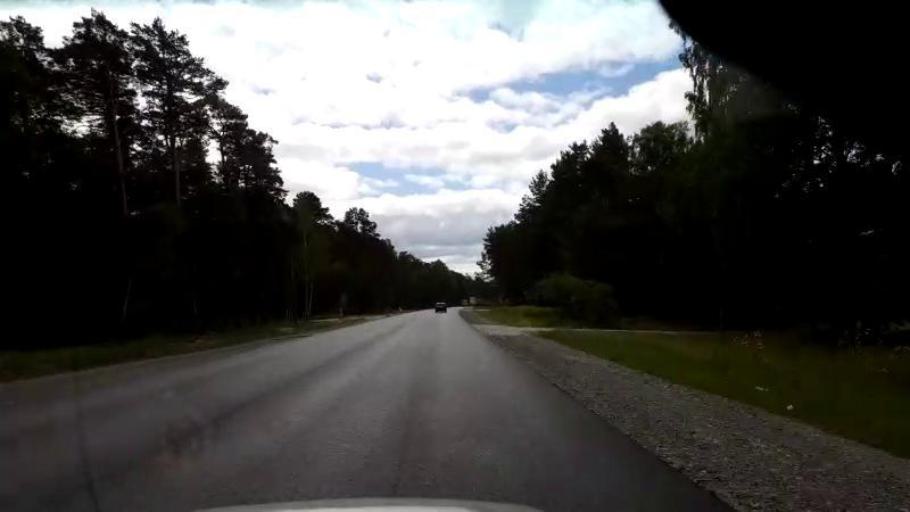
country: LV
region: Salacgrivas
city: Ainazi
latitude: 57.8178
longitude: 24.3471
